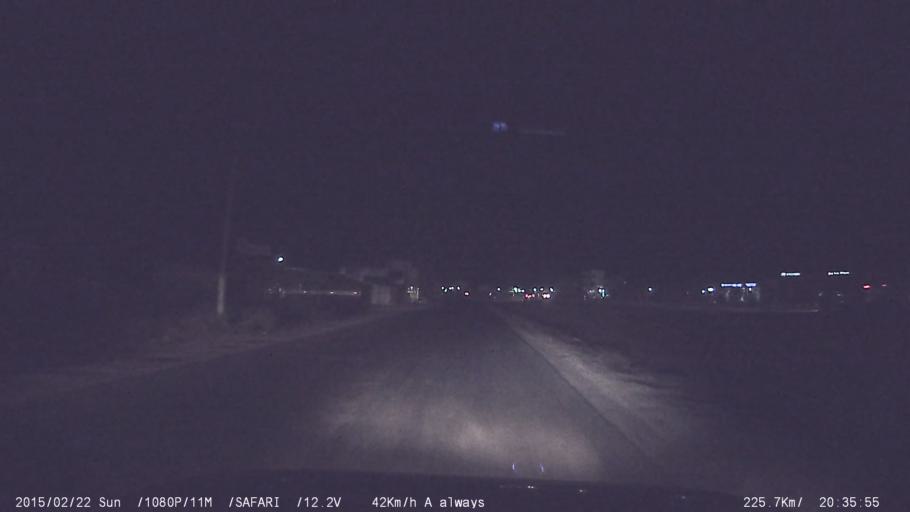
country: IN
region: Tamil Nadu
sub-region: Dindigul
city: Dindigul
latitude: 10.3738
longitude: 77.9527
